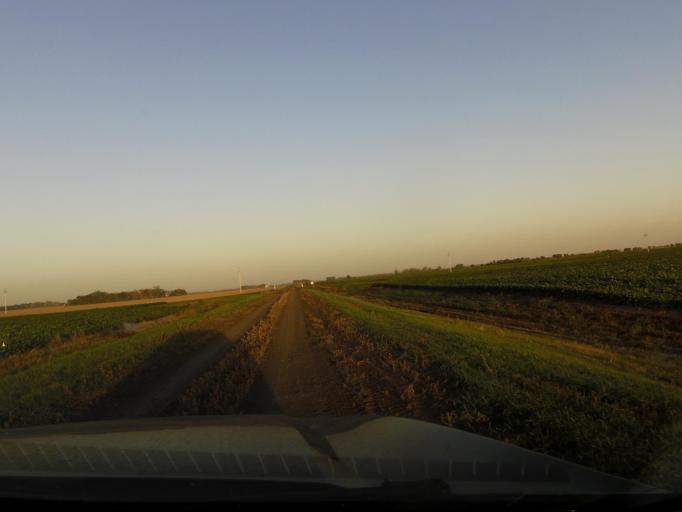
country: US
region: North Dakota
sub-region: Walsh County
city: Grafton
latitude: 48.3832
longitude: -97.2353
